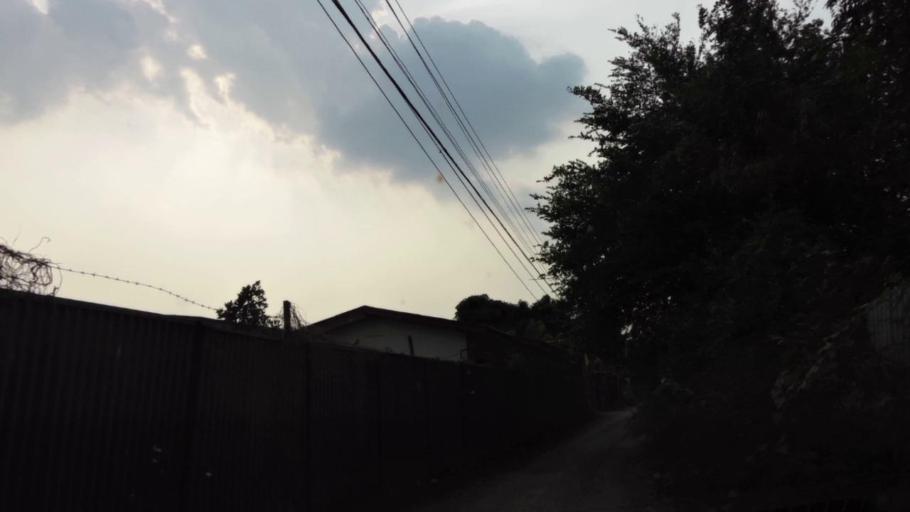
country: TH
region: Phra Nakhon Si Ayutthaya
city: Phra Nakhon Si Ayutthaya
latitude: 14.3503
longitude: 100.5728
